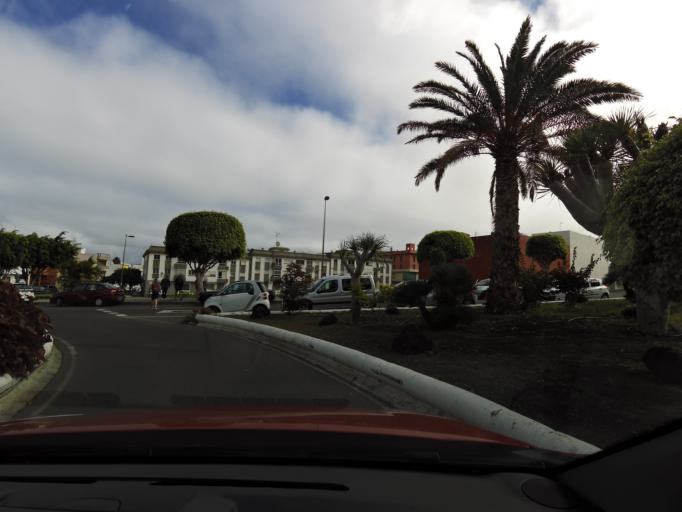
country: ES
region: Canary Islands
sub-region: Provincia de Las Palmas
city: Telde
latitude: 28.0009
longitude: -15.4172
